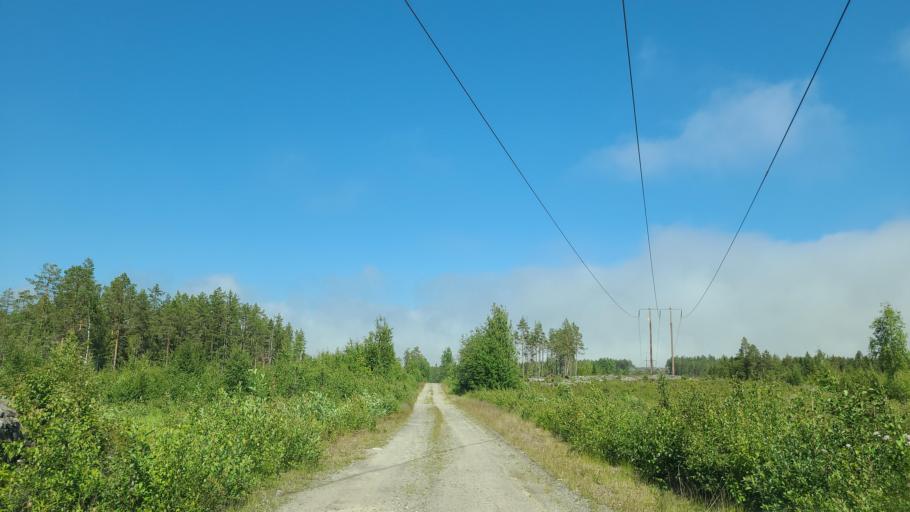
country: SE
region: Vaesternorrland
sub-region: OErnskoeldsviks Kommun
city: Husum
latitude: 63.4412
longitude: 19.2341
